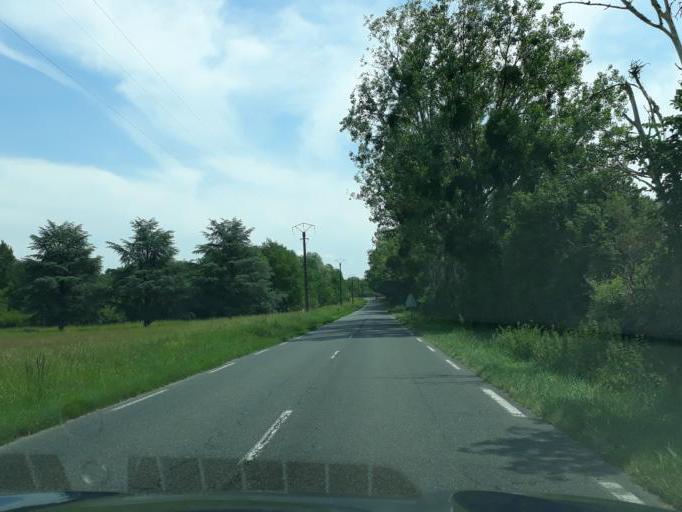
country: FR
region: Centre
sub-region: Departement du Loiret
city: Ferolles
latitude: 47.8060
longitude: 2.0671
